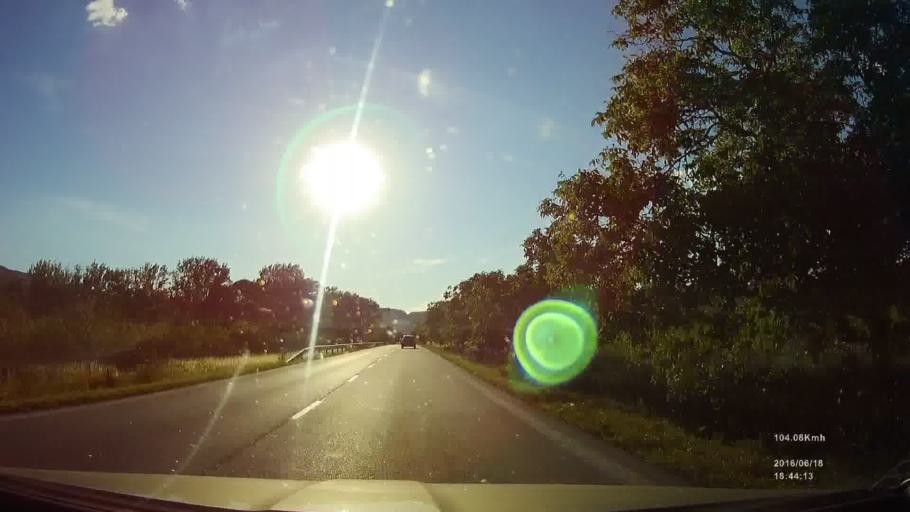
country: SK
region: Kosicky
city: Secovce
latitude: 48.7278
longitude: 21.6001
